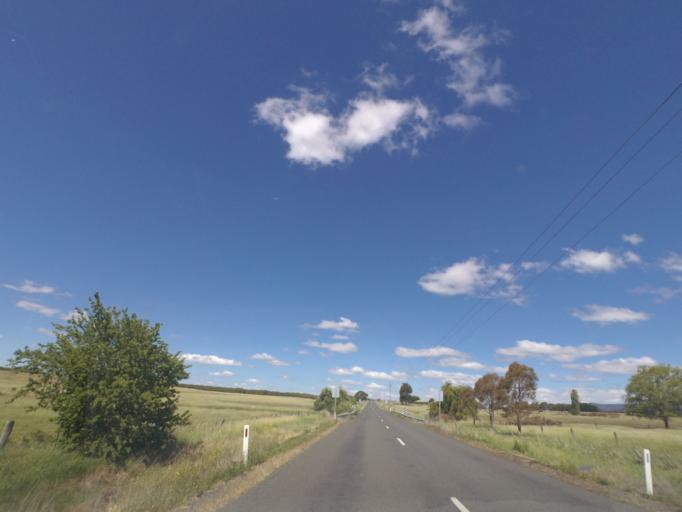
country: AU
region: Victoria
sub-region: Mount Alexander
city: Castlemaine
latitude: -37.2891
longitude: 144.4704
